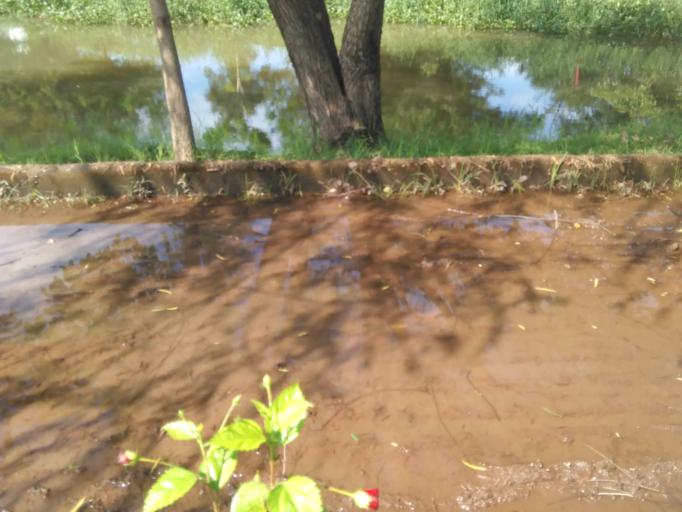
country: MX
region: Nayarit
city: Tepic
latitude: 21.4878
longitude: -104.8596
